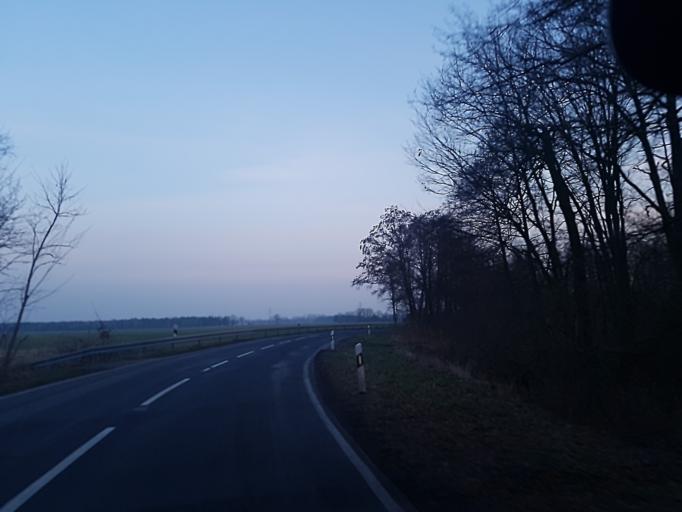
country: DE
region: Saxony-Anhalt
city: Holzdorf
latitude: 51.7743
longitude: 13.0817
